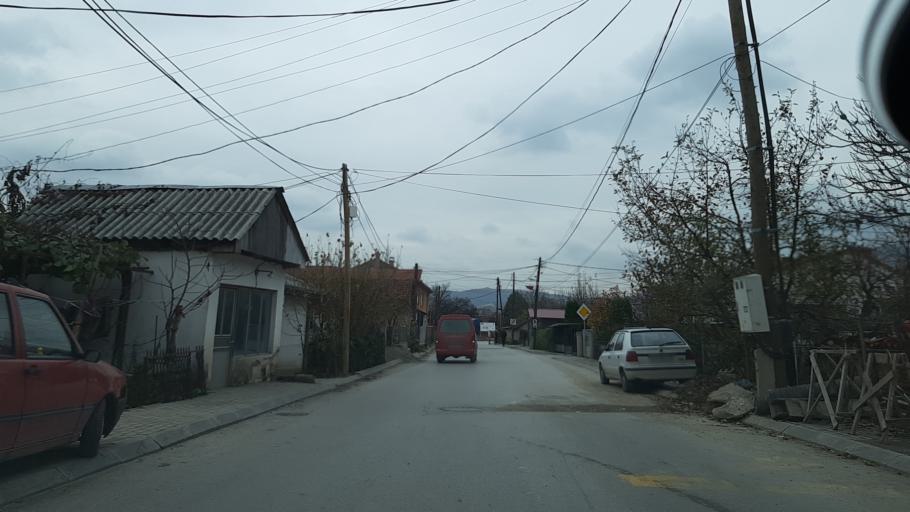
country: MK
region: Kisela Voda
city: Usje
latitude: 41.9750
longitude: 21.4801
